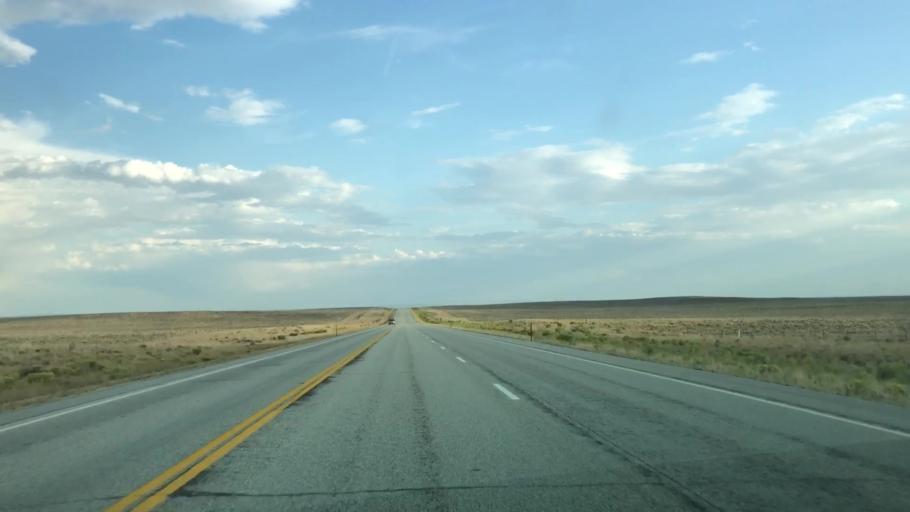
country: US
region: Wyoming
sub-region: Sweetwater County
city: North Rock Springs
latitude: 42.2737
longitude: -109.4810
